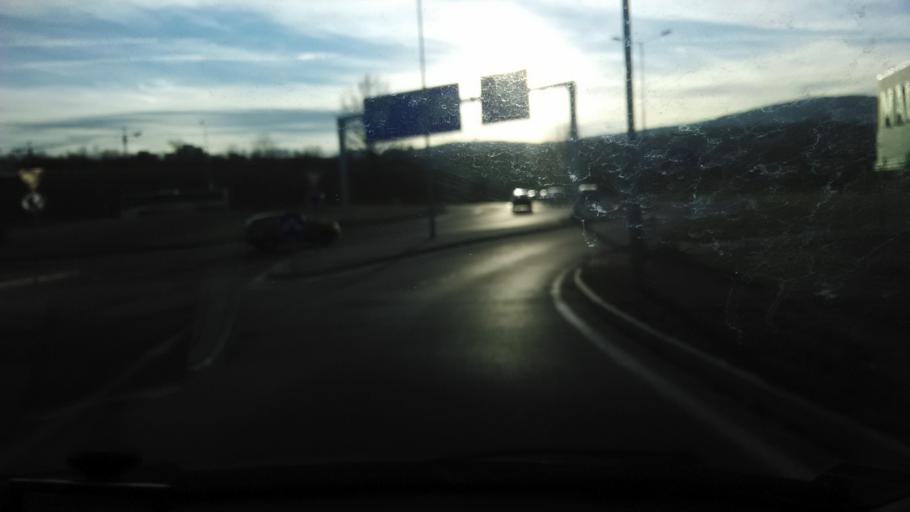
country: SK
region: Bratislavsky
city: Stupava
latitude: 48.2047
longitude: 17.0365
